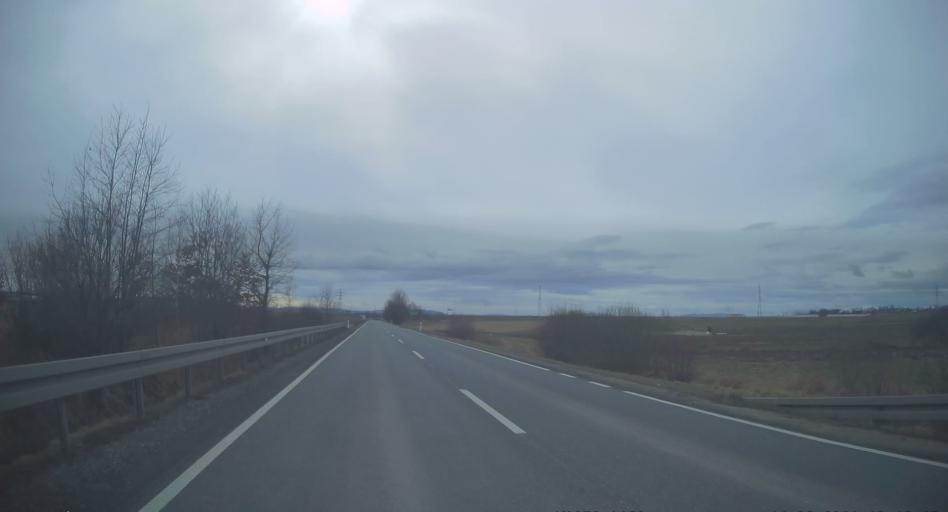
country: PL
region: Lesser Poland Voivodeship
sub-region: Powiat wielicki
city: Szarow
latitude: 49.9957
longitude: 20.2778
